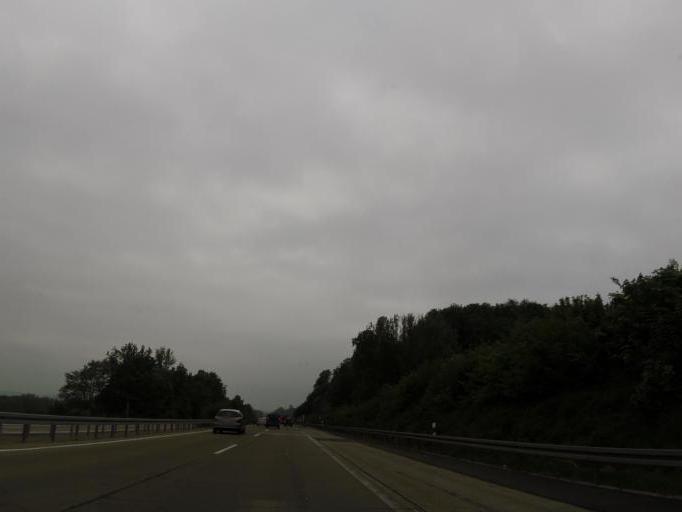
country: DE
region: Lower Saxony
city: Seesen
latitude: 51.8754
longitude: 10.1273
